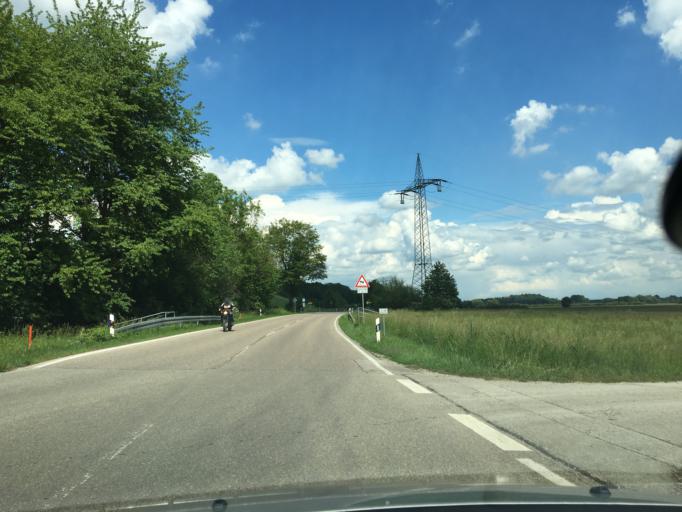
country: DE
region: Bavaria
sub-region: Upper Bavaria
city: Kranzberg
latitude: 48.3854
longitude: 11.6801
